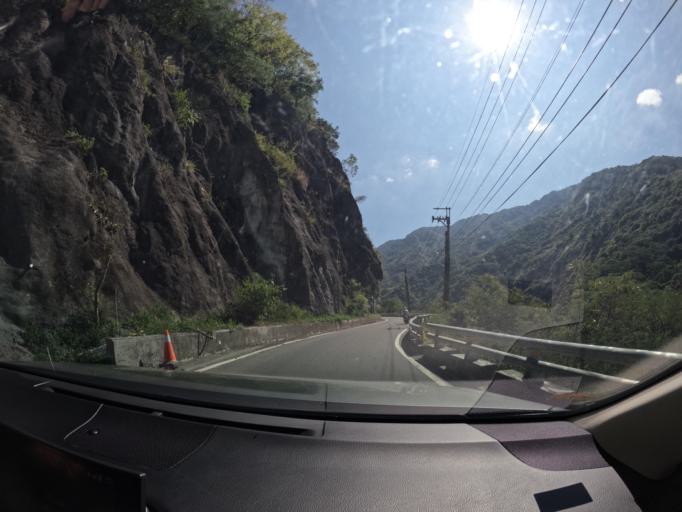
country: TW
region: Taiwan
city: Yujing
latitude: 23.1421
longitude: 120.7415
